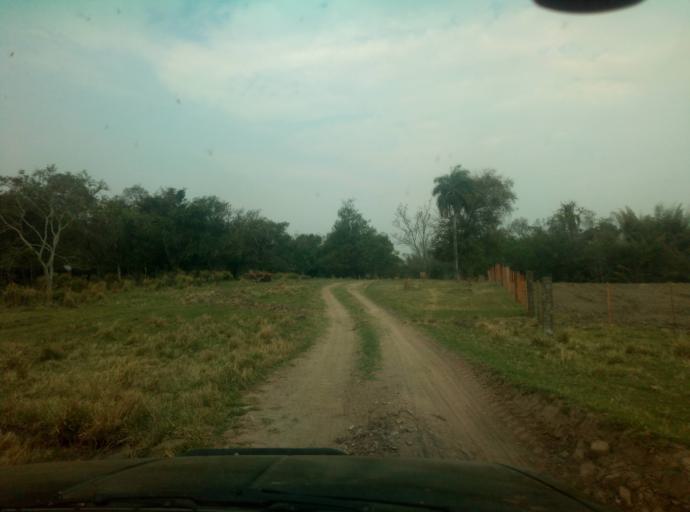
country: PY
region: Caaguazu
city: San Joaquin
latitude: -25.1025
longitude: -56.1228
